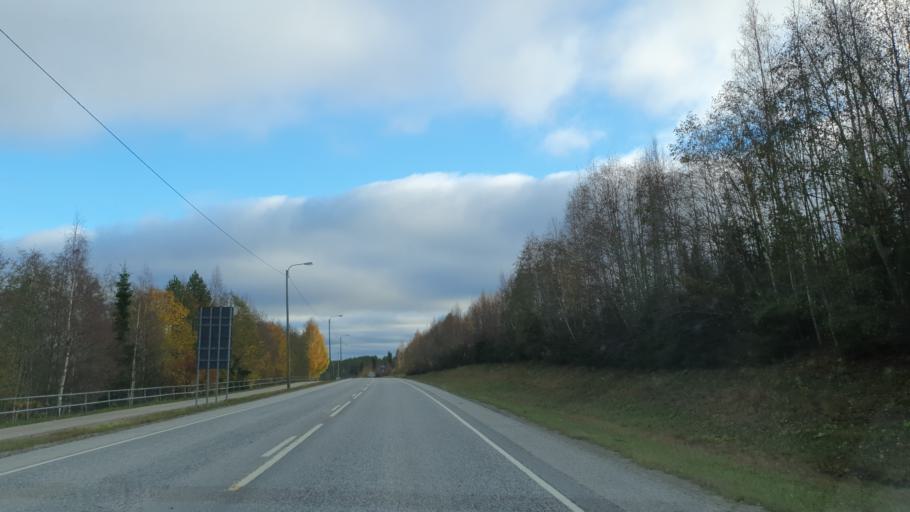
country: FI
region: Kainuu
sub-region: Kajaani
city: Vuokatti
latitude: 64.1349
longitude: 28.2510
